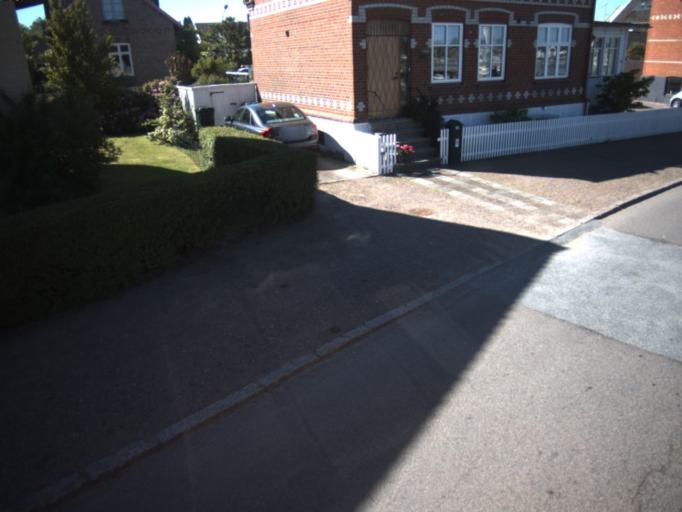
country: SE
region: Skane
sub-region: Helsingborg
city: Rydeback
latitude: 55.9945
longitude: 12.7474
